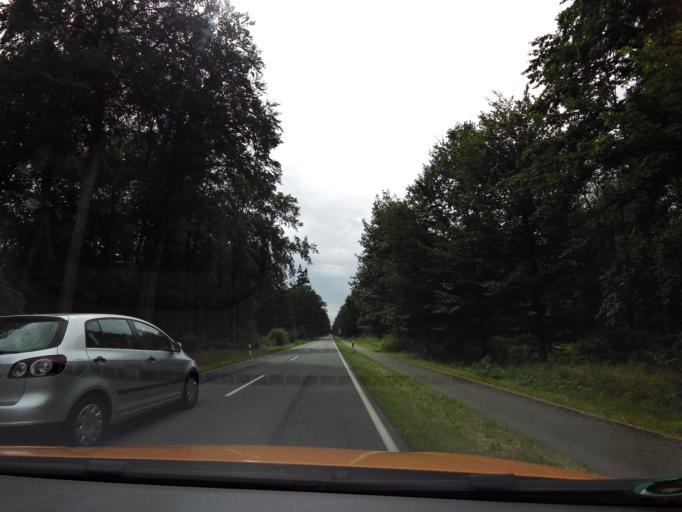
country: DE
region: Lower Saxony
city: Harpstedt
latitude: 52.9302
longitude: 8.6011
